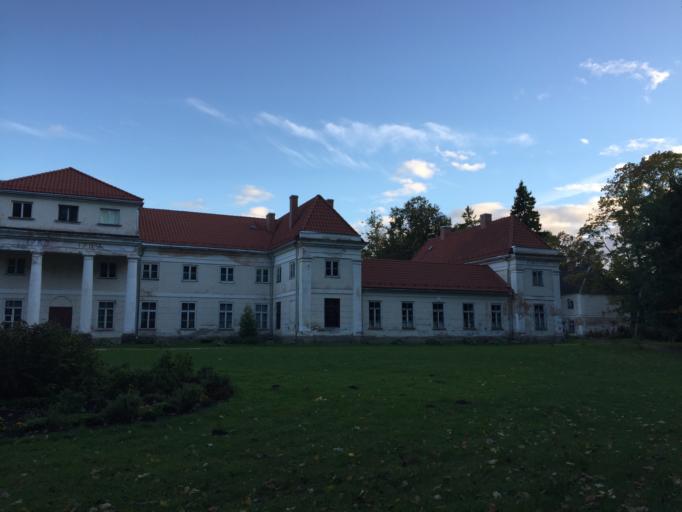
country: LV
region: Varaklani
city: Varaklani
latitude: 56.6082
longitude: 26.7762
